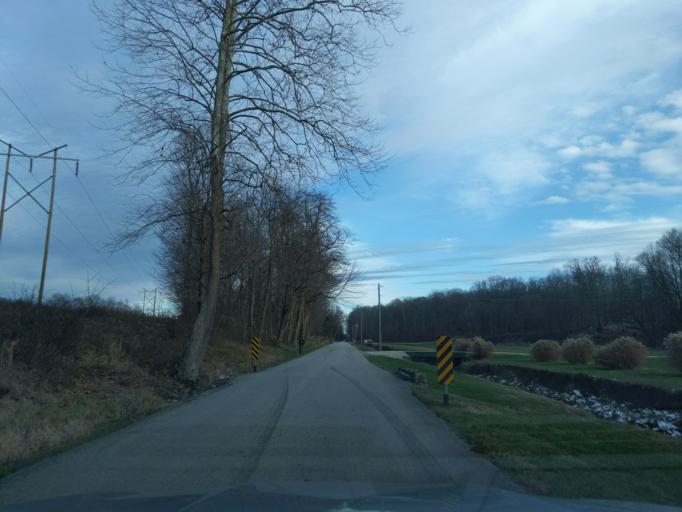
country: US
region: Indiana
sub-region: Decatur County
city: Westport
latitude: 39.2196
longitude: -85.5076
